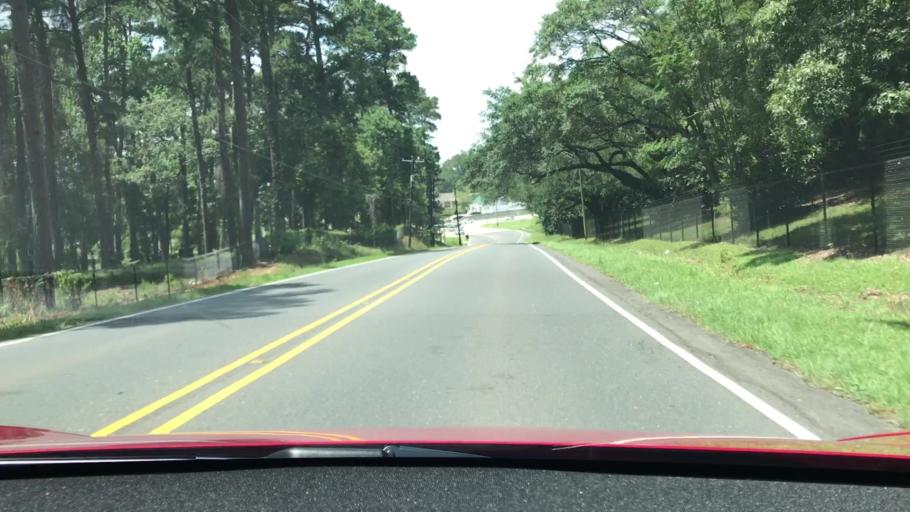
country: US
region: Louisiana
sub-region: Bossier Parish
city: Bossier City
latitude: 32.3921
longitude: -93.7242
